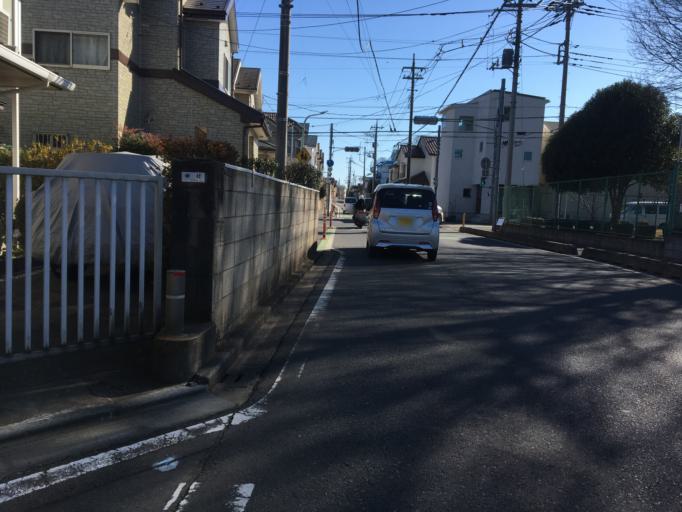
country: JP
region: Saitama
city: Oi
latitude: 35.8382
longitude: 139.5198
